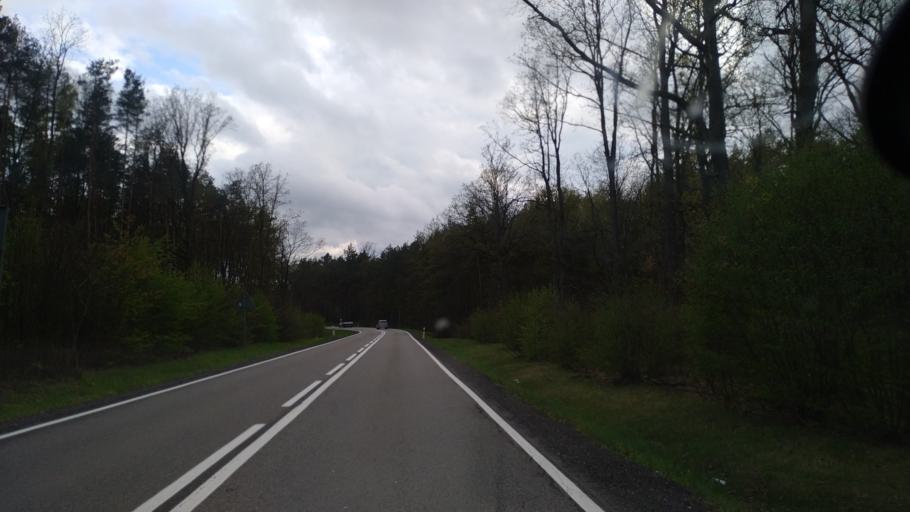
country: PL
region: Pomeranian Voivodeship
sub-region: Powiat kwidzynski
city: Ryjewo
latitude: 53.8351
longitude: 18.9929
